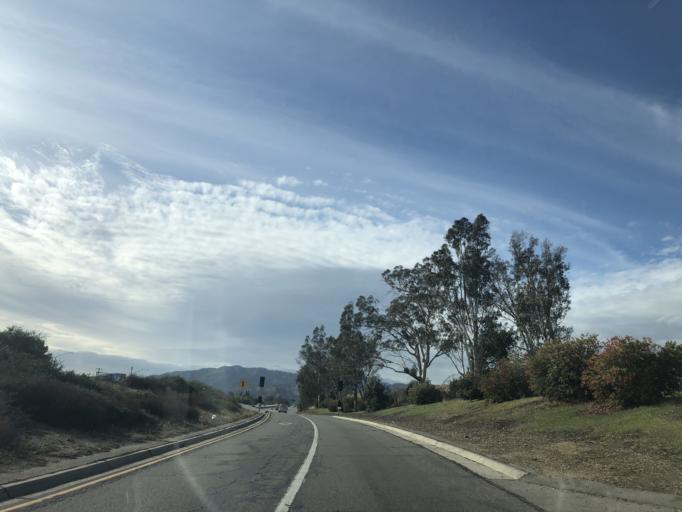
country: US
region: California
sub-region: Los Angeles County
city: San Fernando
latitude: 34.3242
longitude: -118.4615
